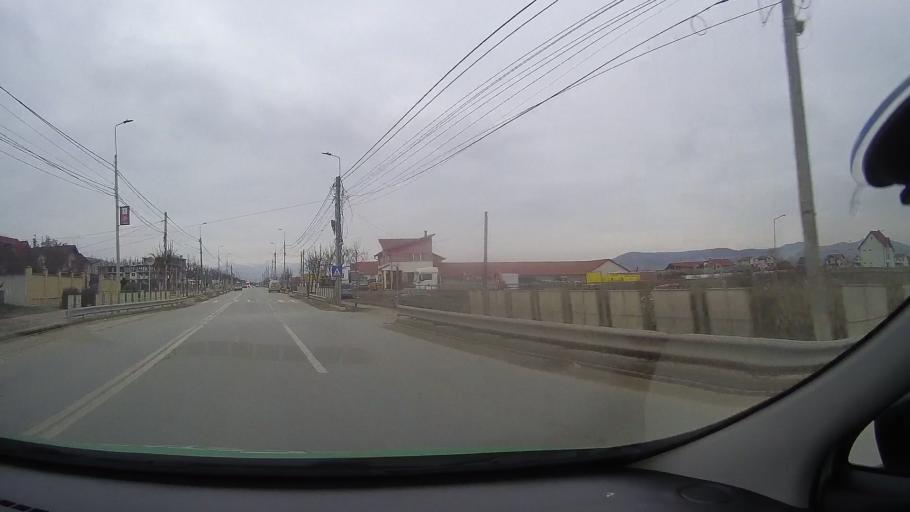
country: RO
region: Alba
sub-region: Municipiul Alba Iulia
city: Micesti
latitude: 46.0933
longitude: 23.5540
